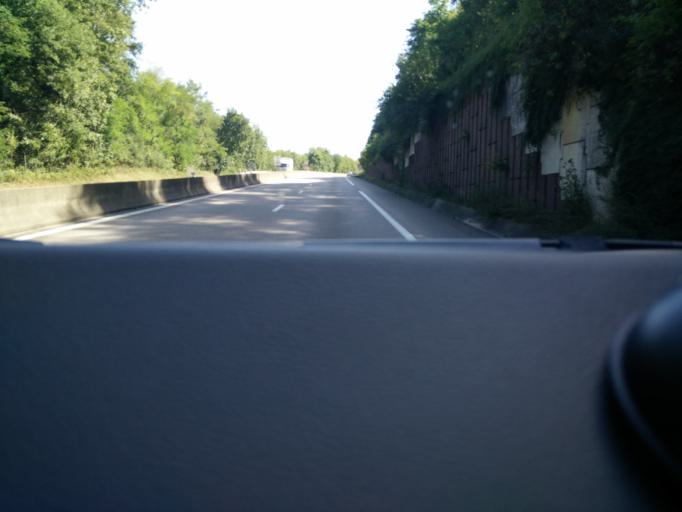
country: FR
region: Lorraine
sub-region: Departement des Vosges
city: Saint-Die-des-Vosges
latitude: 48.2824
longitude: 6.9361
